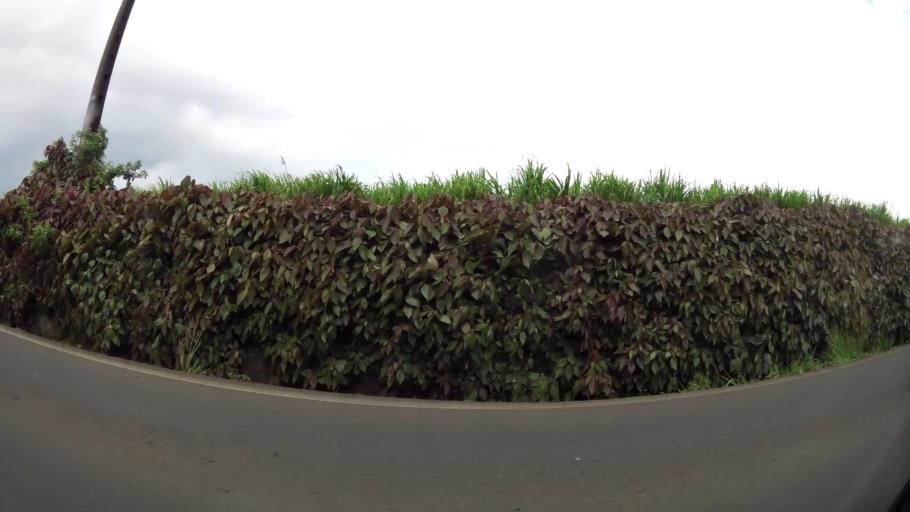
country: RE
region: Reunion
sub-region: Reunion
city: Sainte-Suzanne
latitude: -20.9080
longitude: 55.5983
